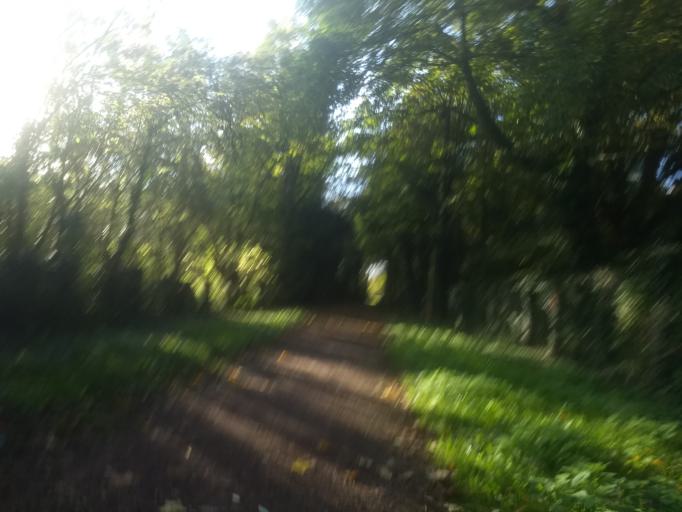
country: FR
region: Nord-Pas-de-Calais
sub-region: Departement du Pas-de-Calais
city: Saint-Laurent-Blangy
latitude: 50.3031
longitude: 2.8160
